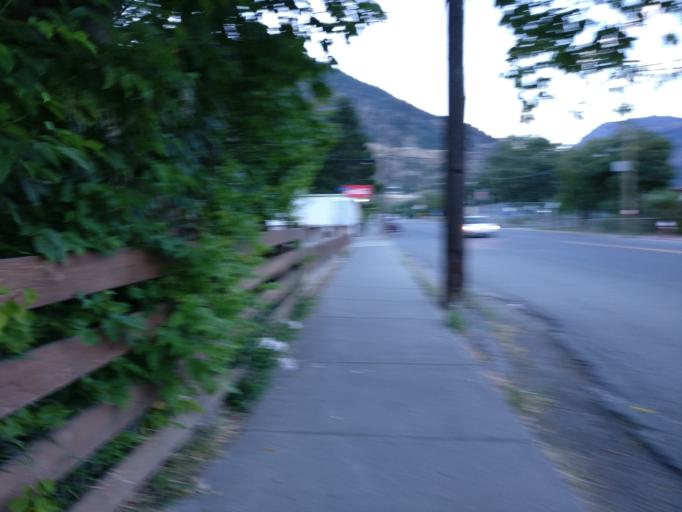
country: CA
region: British Columbia
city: Lillooet
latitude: 50.6875
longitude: -121.9371
